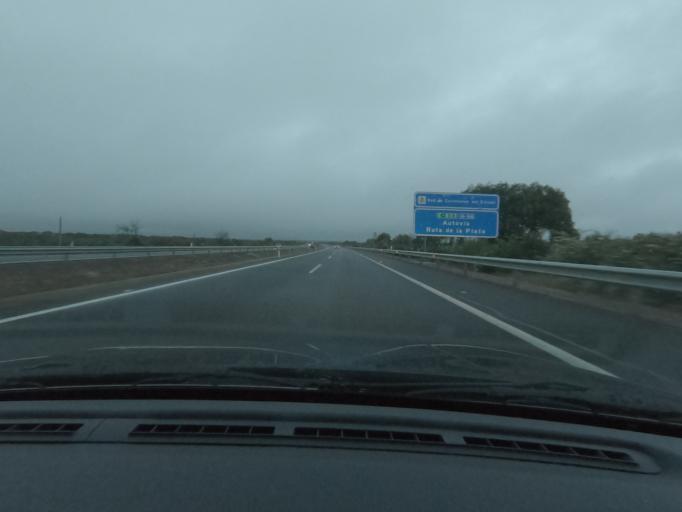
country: ES
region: Extremadura
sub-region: Provincia de Badajoz
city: Aljucen
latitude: 39.1023
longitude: -6.2839
